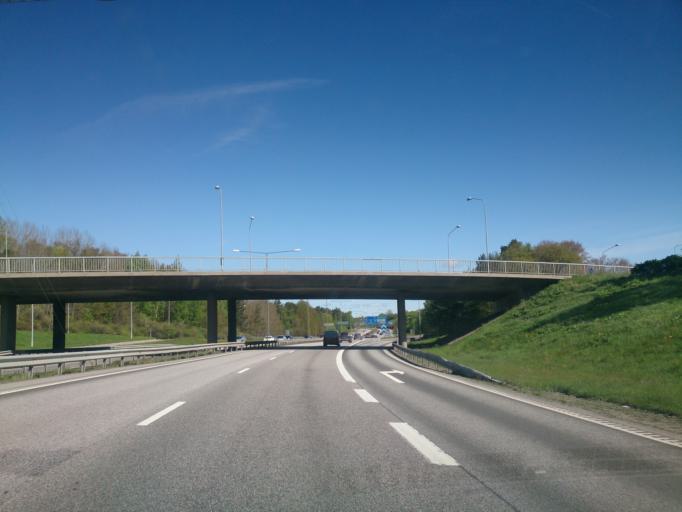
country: SE
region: Stockholm
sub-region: Stockholms Kommun
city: Arsta
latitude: 59.2500
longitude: 18.0992
